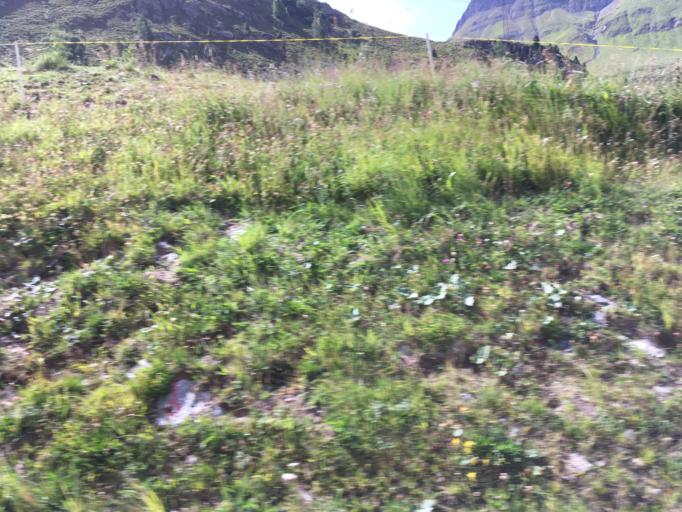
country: CH
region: Grisons
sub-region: Maloja District
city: Silvaplana
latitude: 46.4639
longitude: 9.6863
